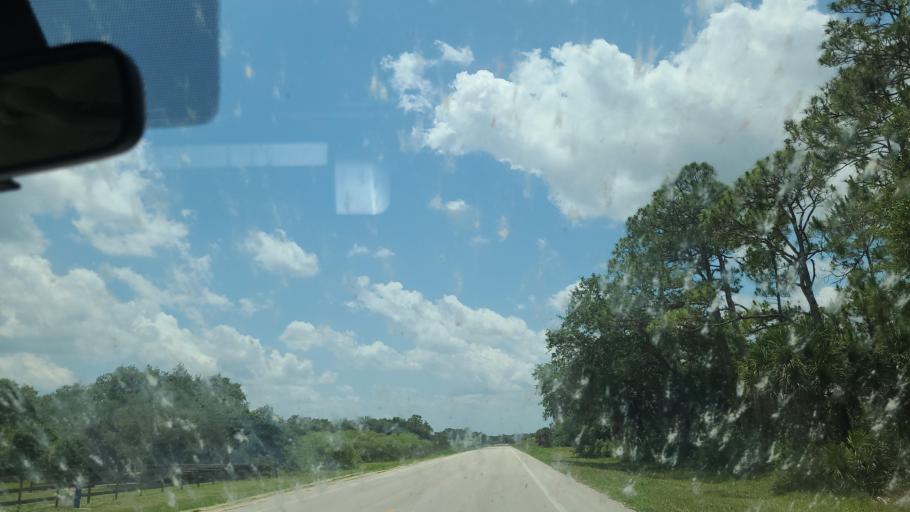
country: US
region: Florida
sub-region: Glades County
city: Buckhead Ridge
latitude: 27.1060
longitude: -81.0693
